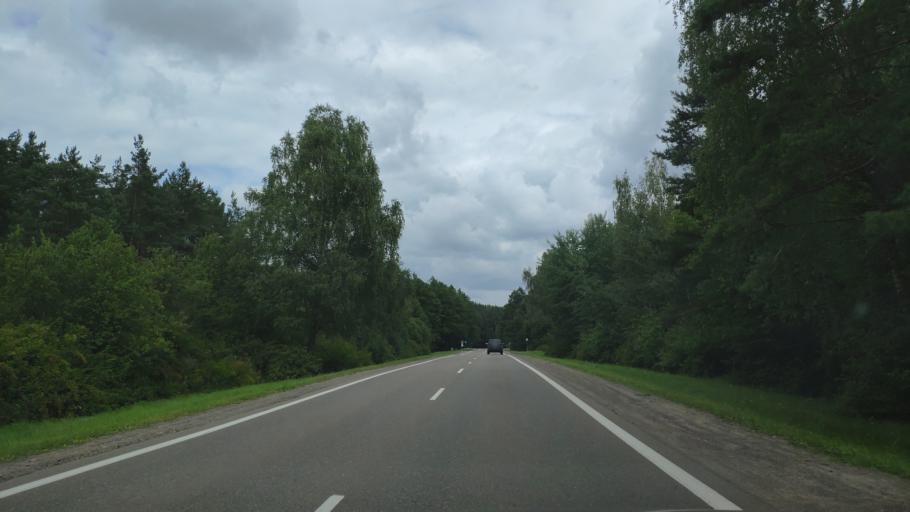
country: BY
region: Minsk
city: Syomkava
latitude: 53.9756
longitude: 27.4399
